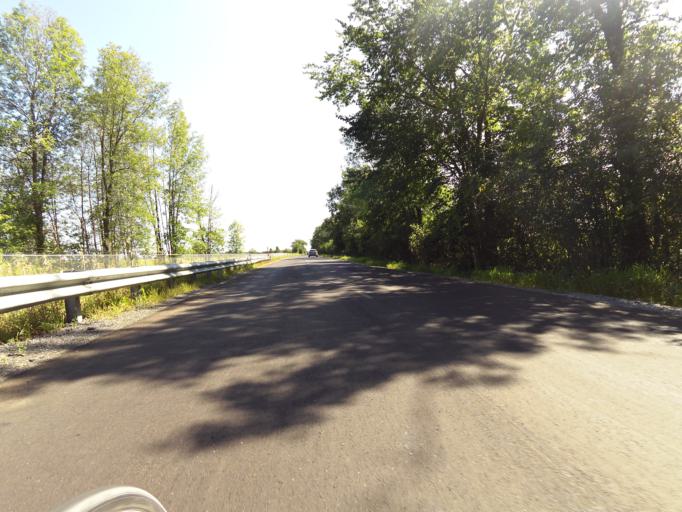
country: CA
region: Ontario
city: Bells Corners
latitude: 45.3706
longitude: -75.9288
